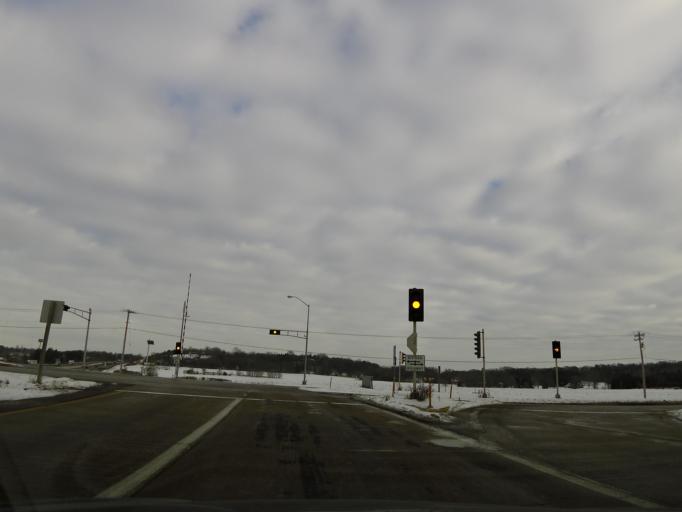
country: US
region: Wisconsin
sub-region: Saint Croix County
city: Hudson
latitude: 44.9626
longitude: -92.6807
